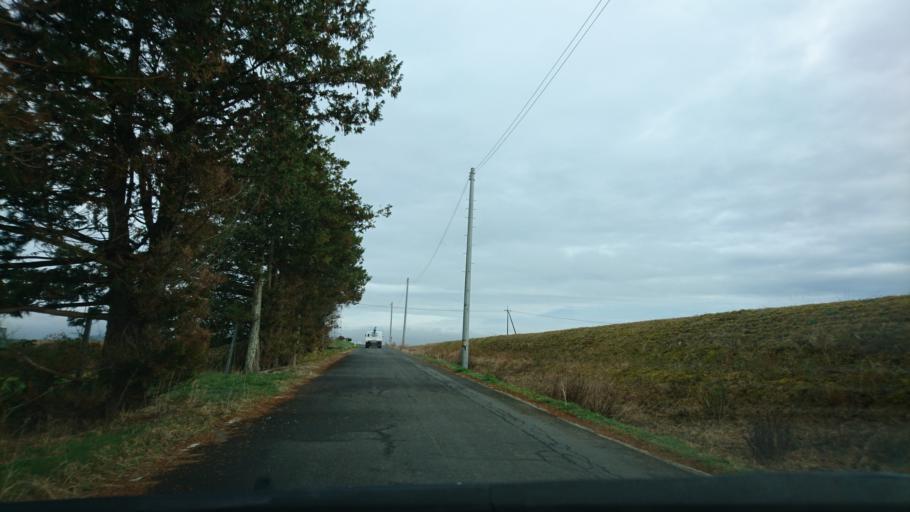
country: JP
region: Iwate
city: Ichinoseki
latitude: 38.8850
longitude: 141.1933
